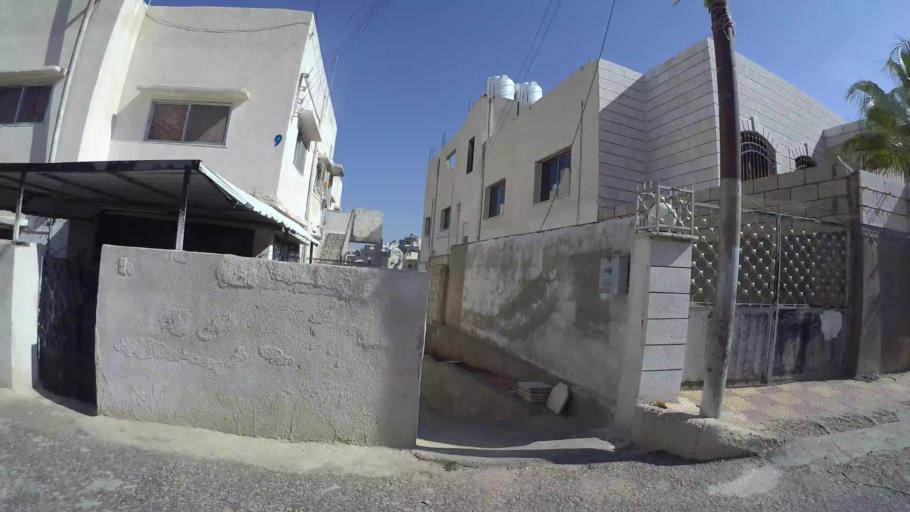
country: JO
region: Amman
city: Amman
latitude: 31.9877
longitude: 35.9866
